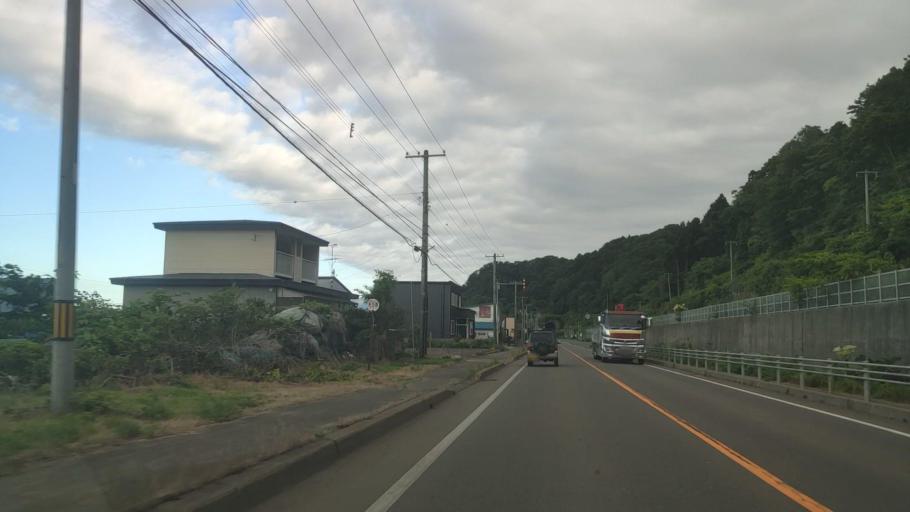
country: JP
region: Hokkaido
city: Nanae
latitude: 42.1599
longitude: 140.4723
